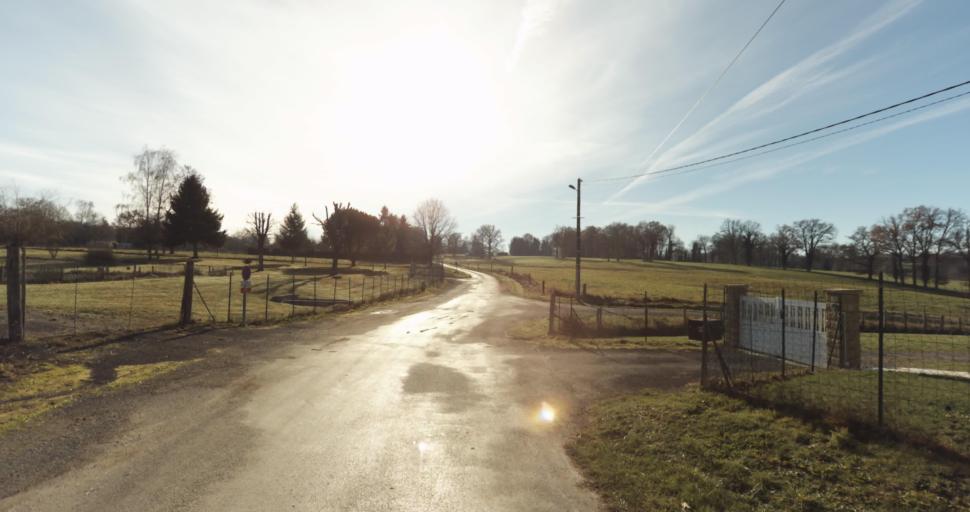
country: FR
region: Limousin
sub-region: Departement de la Haute-Vienne
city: Sereilhac
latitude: 45.7866
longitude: 1.0935
